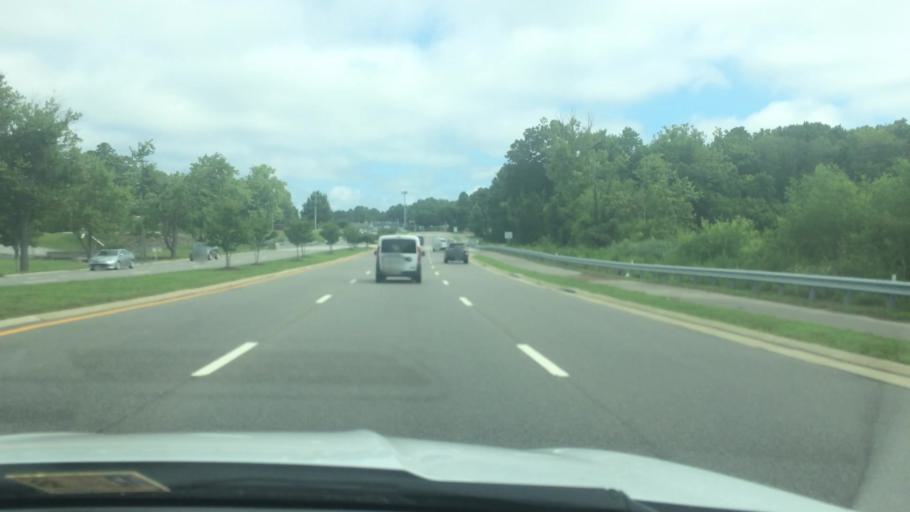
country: US
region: Virginia
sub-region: City of Poquoson
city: Poquoson
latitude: 37.1362
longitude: -76.4572
